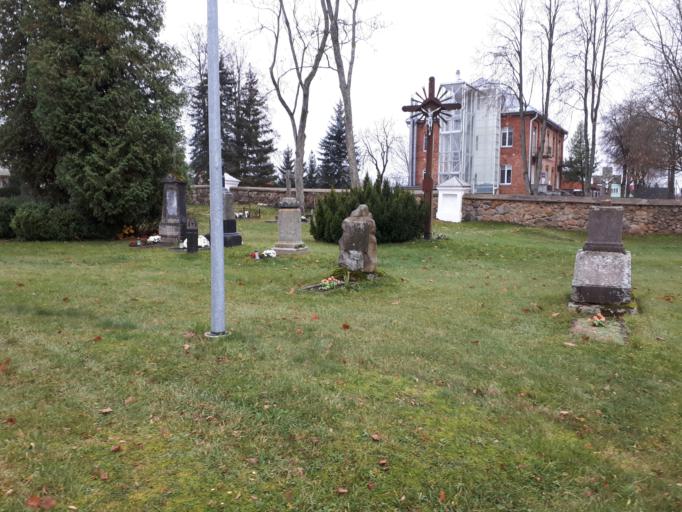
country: LT
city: Aukstadvaris
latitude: 54.4858
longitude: 24.5947
